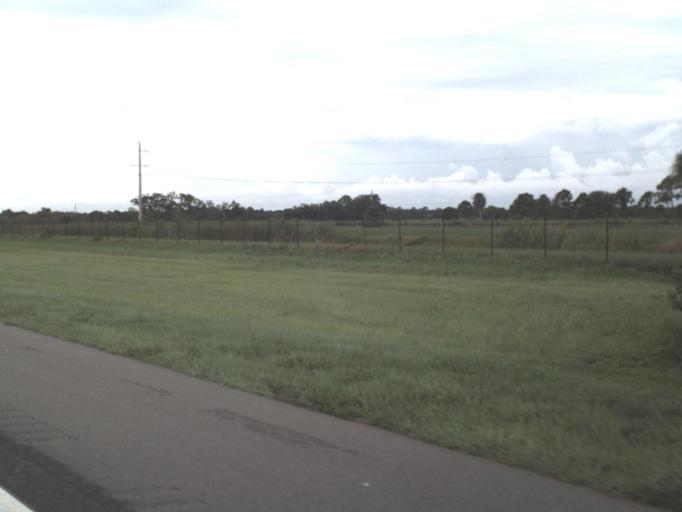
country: US
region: Florida
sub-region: Sarasota County
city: Laurel
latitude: 27.1791
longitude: -82.4362
